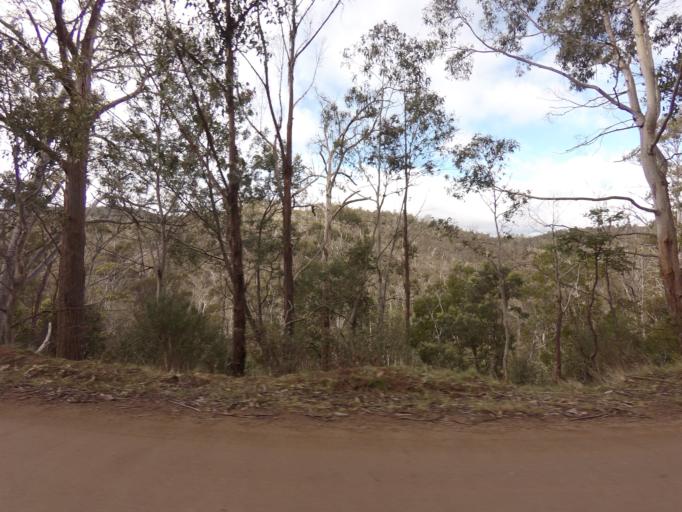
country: AU
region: Tasmania
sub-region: Derwent Valley
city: New Norfolk
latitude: -42.7411
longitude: 146.8675
